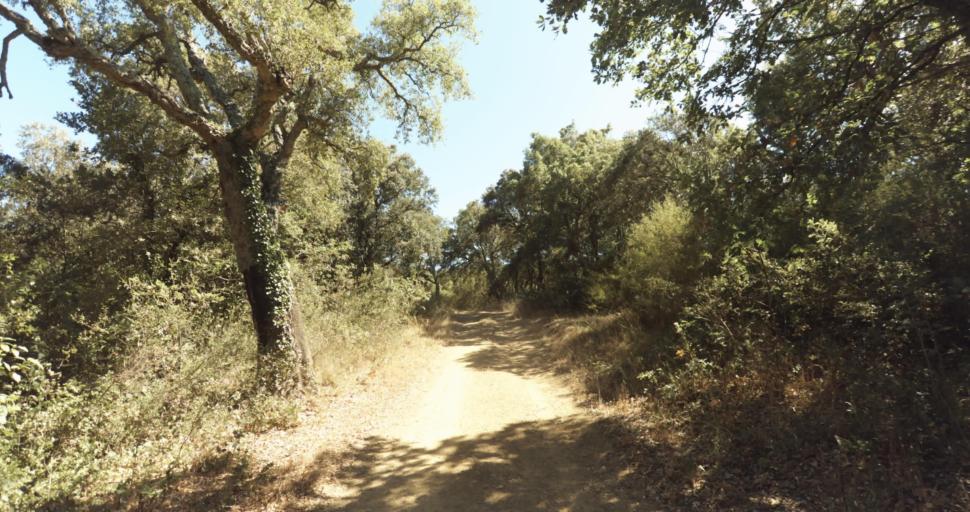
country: FR
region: Provence-Alpes-Cote d'Azur
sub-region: Departement du Var
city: Gassin
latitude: 43.2436
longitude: 6.5843
